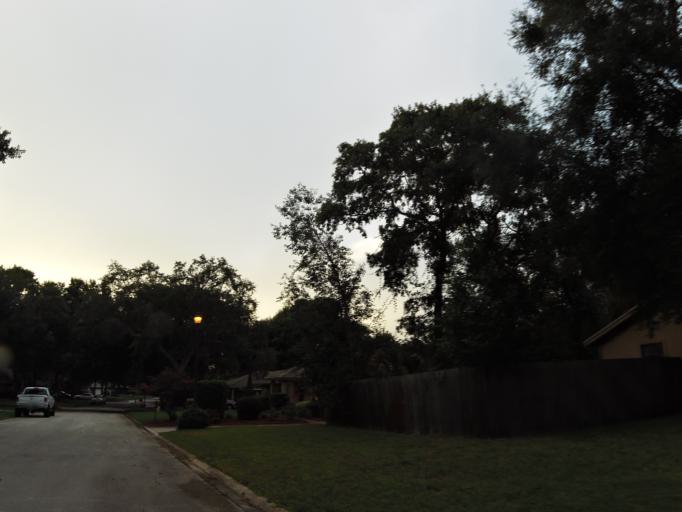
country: US
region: Florida
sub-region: Duval County
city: Atlantic Beach
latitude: 30.3572
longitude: -81.4944
